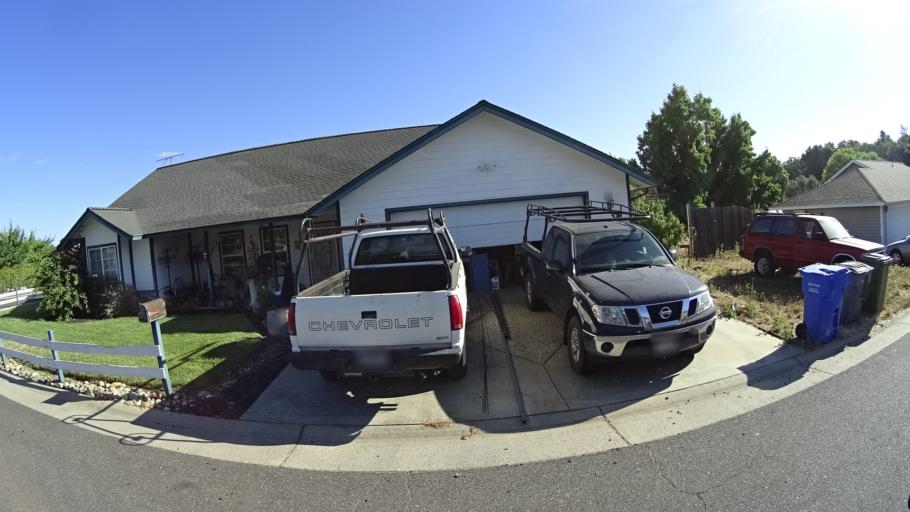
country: US
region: California
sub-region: Calaveras County
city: San Andreas
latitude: 38.1869
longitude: -120.6709
